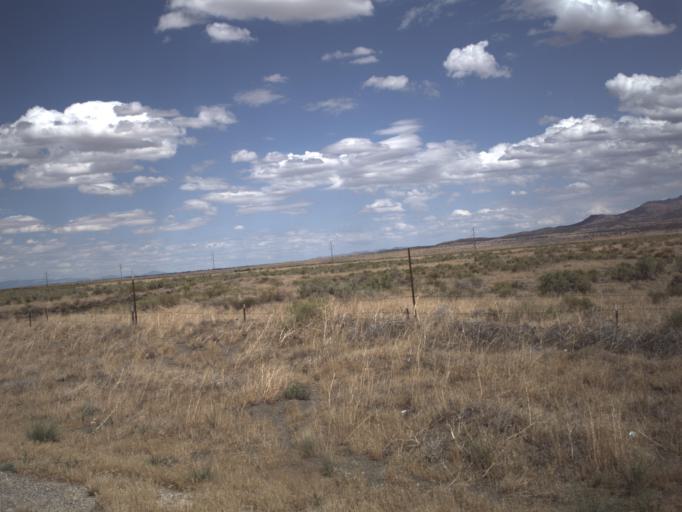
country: US
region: Utah
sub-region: Millard County
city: Delta
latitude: 39.2364
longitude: -112.4305
